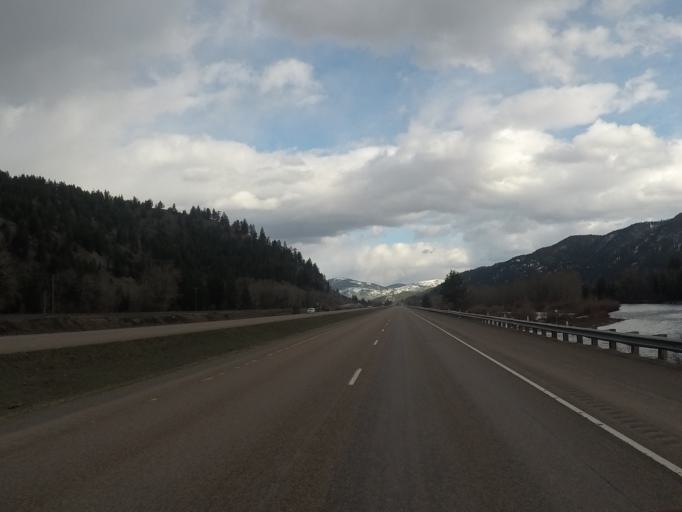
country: US
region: Montana
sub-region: Missoula County
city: Clinton
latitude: 46.8179
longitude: -113.7982
